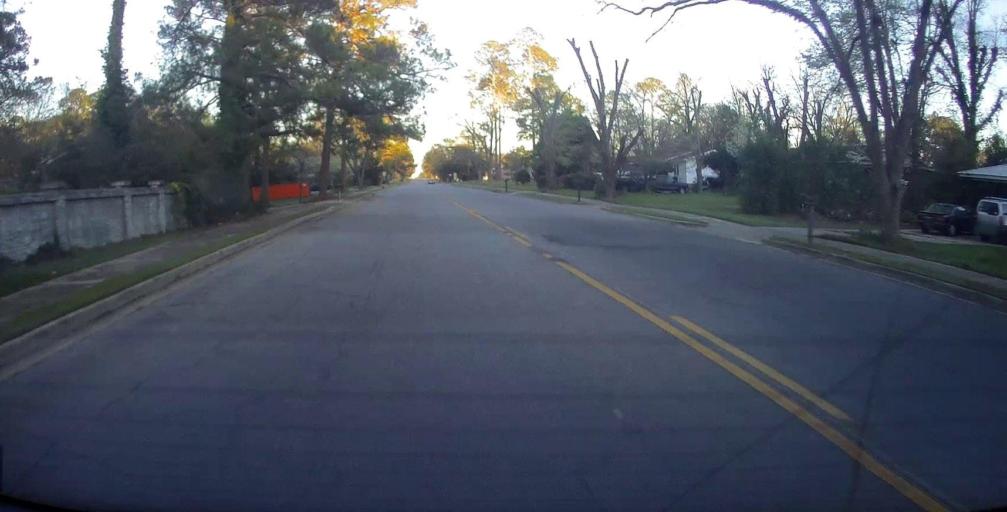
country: US
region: Georgia
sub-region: Crisp County
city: Cordele
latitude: 31.9550
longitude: -83.7747
